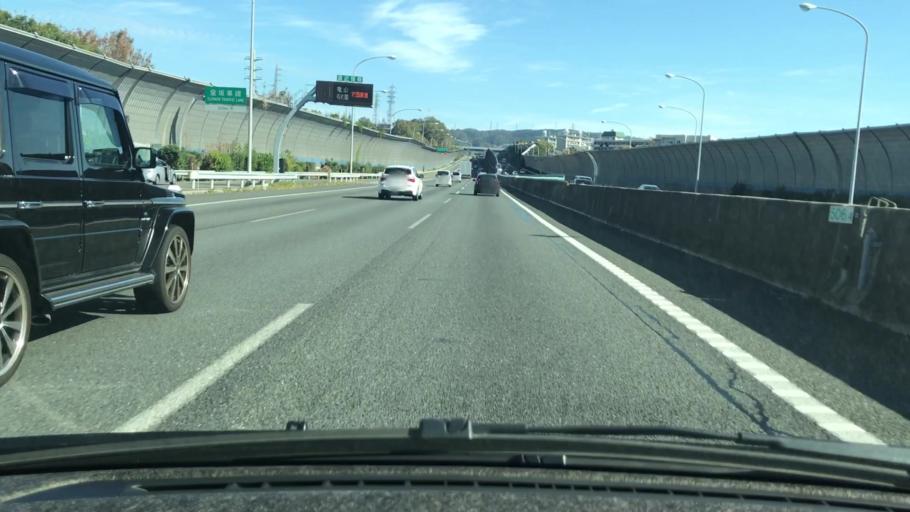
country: JP
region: Osaka
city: Takatsuki
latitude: 34.8613
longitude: 135.6029
